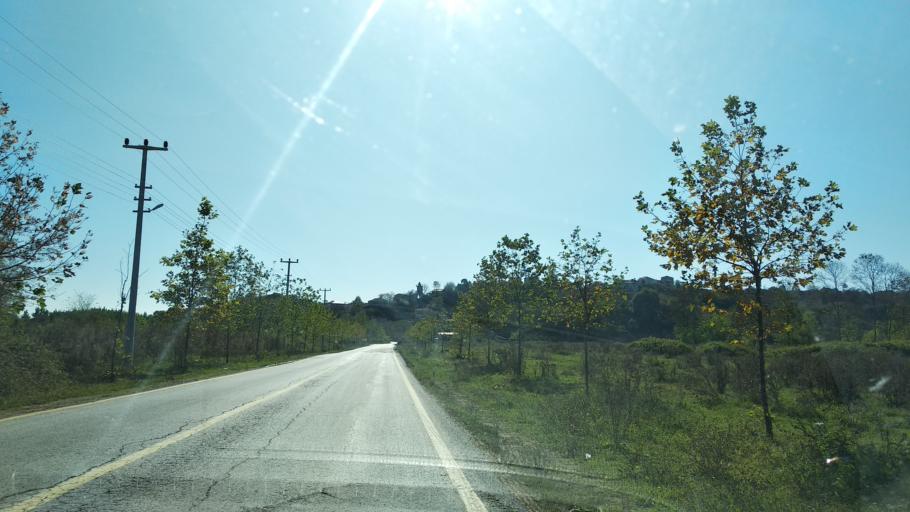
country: TR
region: Sakarya
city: Karasu
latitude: 41.1105
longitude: 30.6422
